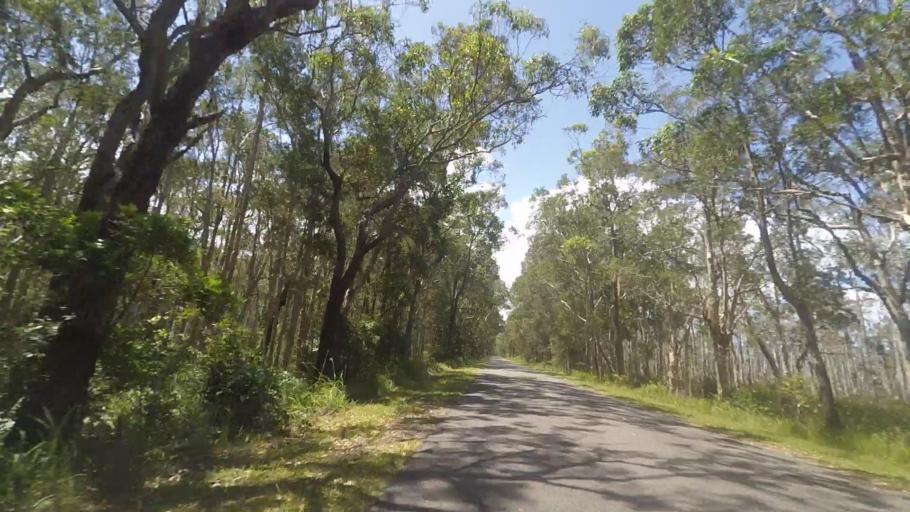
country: AU
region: New South Wales
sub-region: Great Lakes
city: Bulahdelah
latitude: -32.5272
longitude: 152.3228
